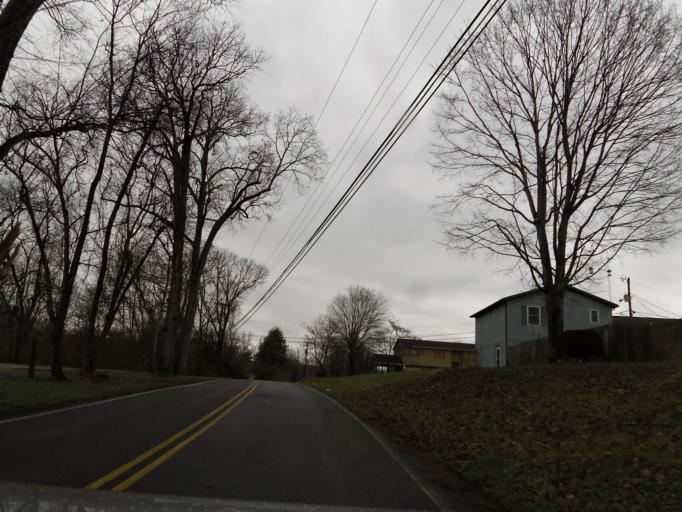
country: US
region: Tennessee
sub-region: Knox County
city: Knoxville
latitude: 35.9778
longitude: -84.0036
